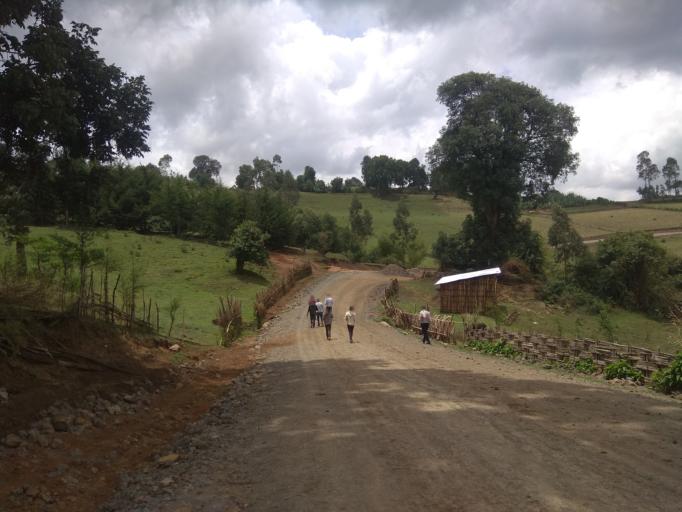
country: ET
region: Oromiya
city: Guder
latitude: 8.7493
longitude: 37.6299
